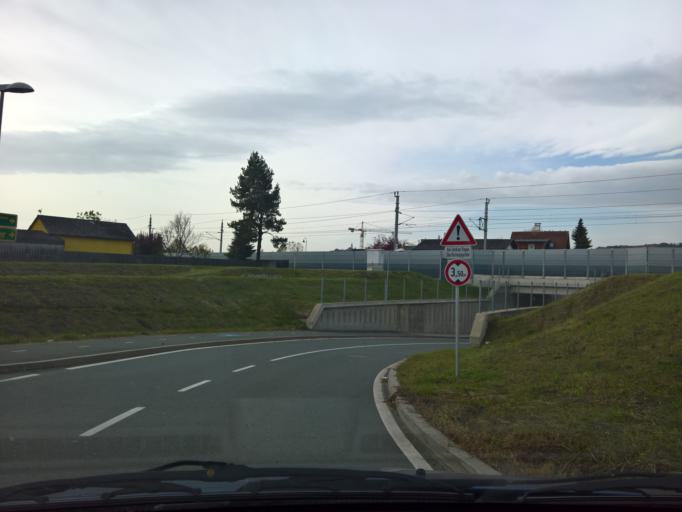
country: AT
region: Styria
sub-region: Politischer Bezirk Leibnitz
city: Kaindorf an der Sulm
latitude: 46.7902
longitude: 15.5451
